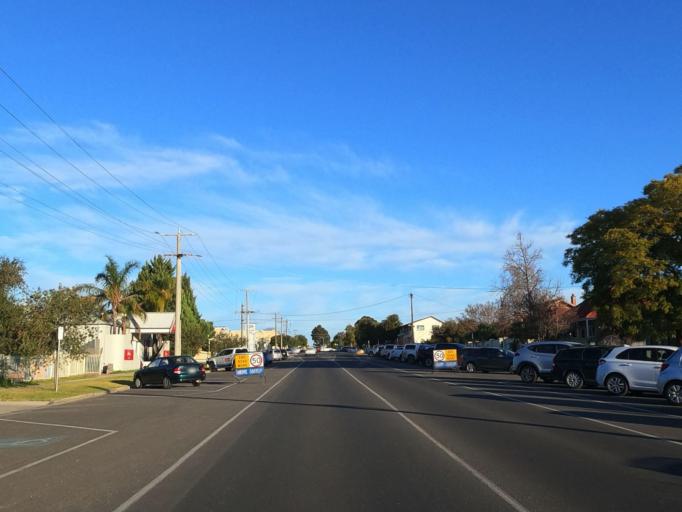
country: AU
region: Victoria
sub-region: Swan Hill
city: Swan Hill
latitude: -35.3355
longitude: 143.5571
